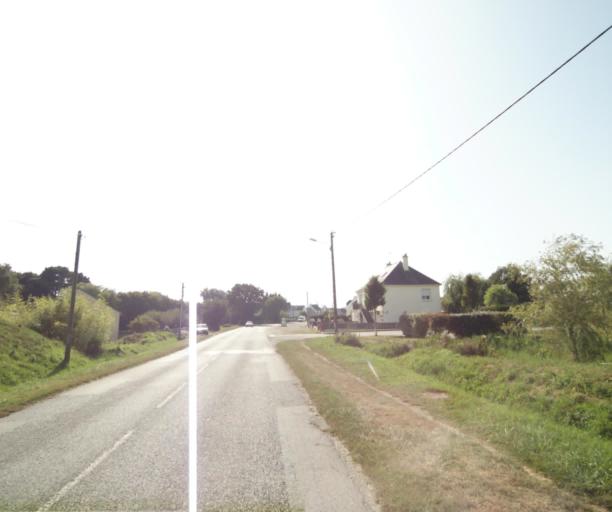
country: FR
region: Brittany
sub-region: Departement du Morbihan
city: Riantec
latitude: 47.7151
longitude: -3.3059
